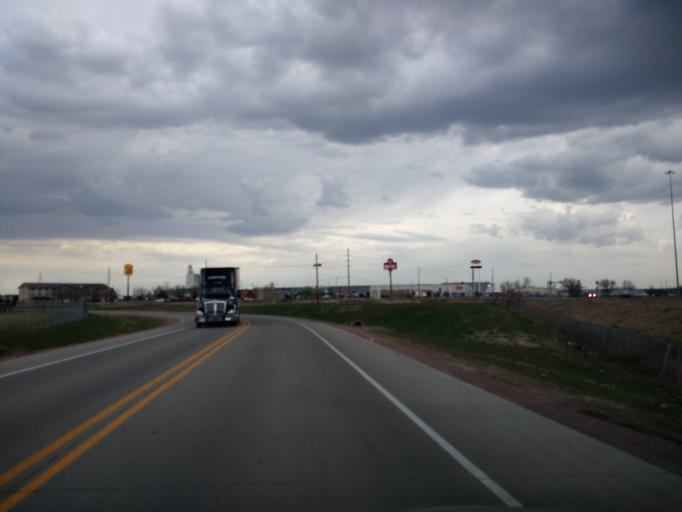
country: US
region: Iowa
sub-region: Woodbury County
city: Sergeant Bluff
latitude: 42.4321
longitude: -96.3754
